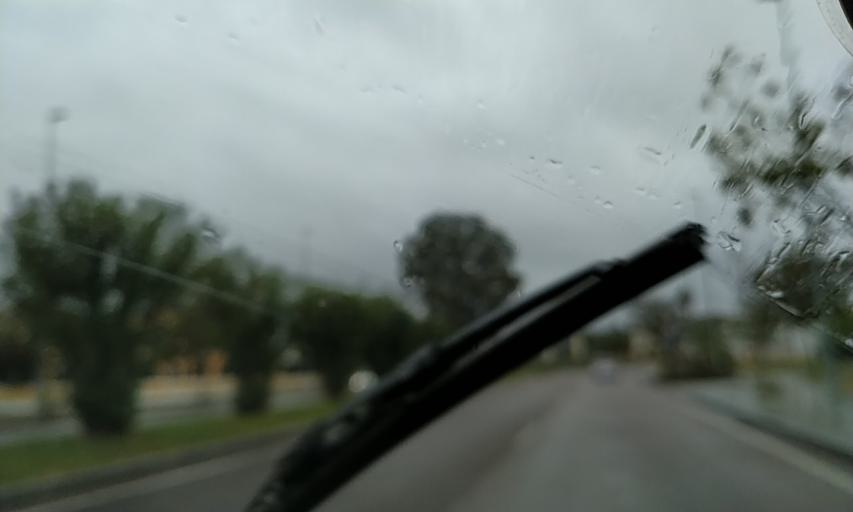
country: ES
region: Extremadura
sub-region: Provincia de Badajoz
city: Badajoz
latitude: 38.8962
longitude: -6.9699
